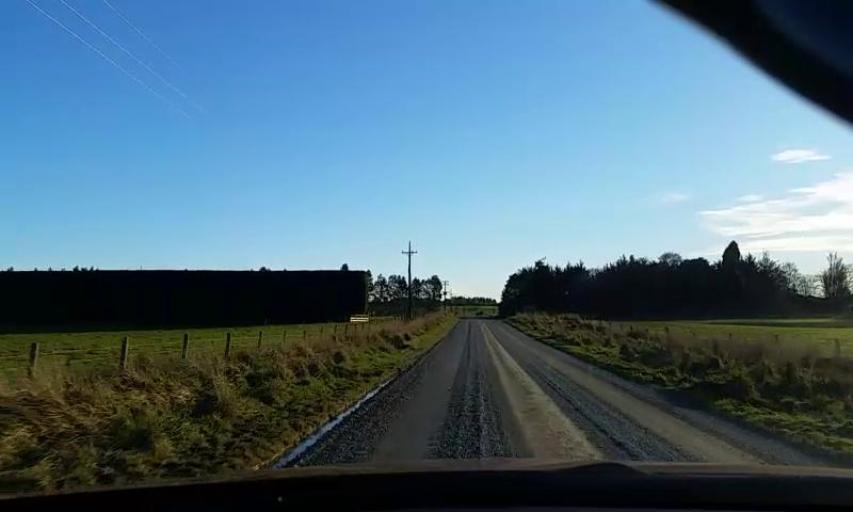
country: NZ
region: Southland
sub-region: Invercargill City
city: Invercargill
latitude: -46.2916
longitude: 168.4161
